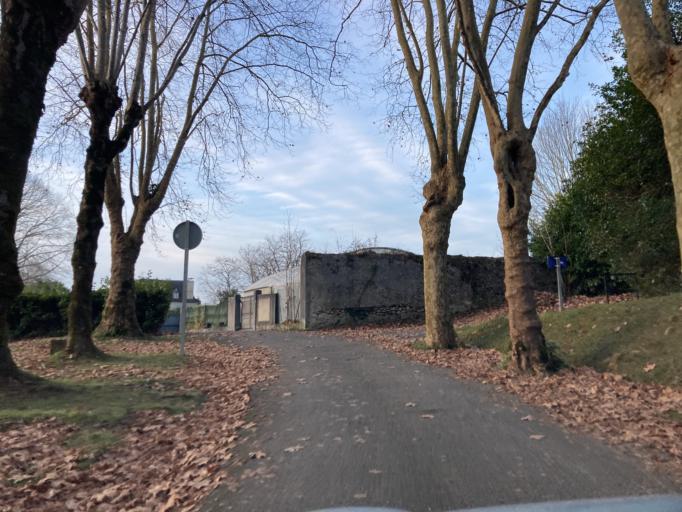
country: FR
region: Aquitaine
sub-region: Departement des Pyrenees-Atlantiques
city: Oloron-Sainte-Marie
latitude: 43.1925
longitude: -0.6006
